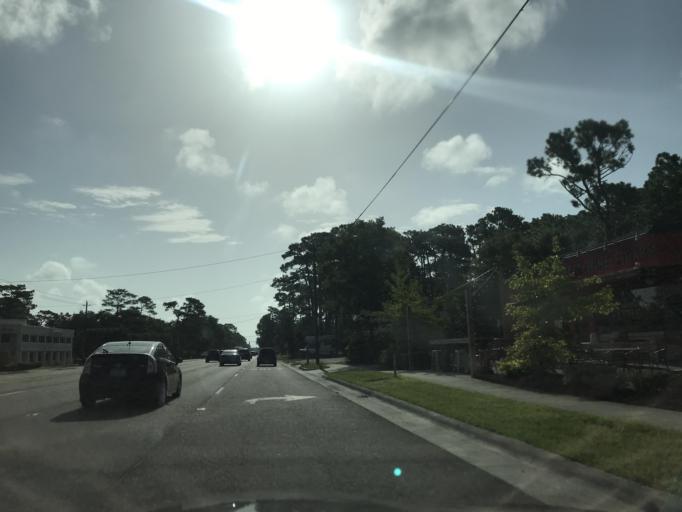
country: US
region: North Carolina
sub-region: New Hanover County
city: Seagate
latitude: 34.2100
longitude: -77.8838
